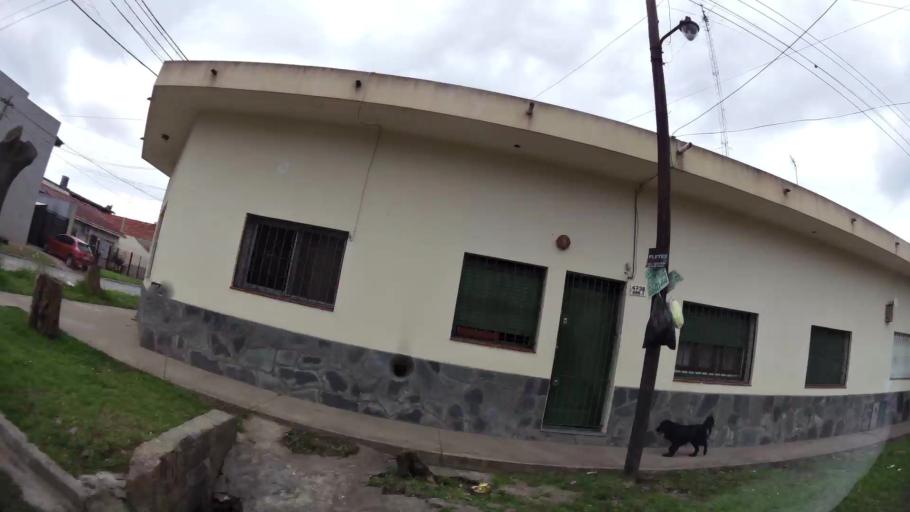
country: AR
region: Buenos Aires
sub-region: Partido de Quilmes
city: Quilmes
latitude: -34.7693
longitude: -58.2763
